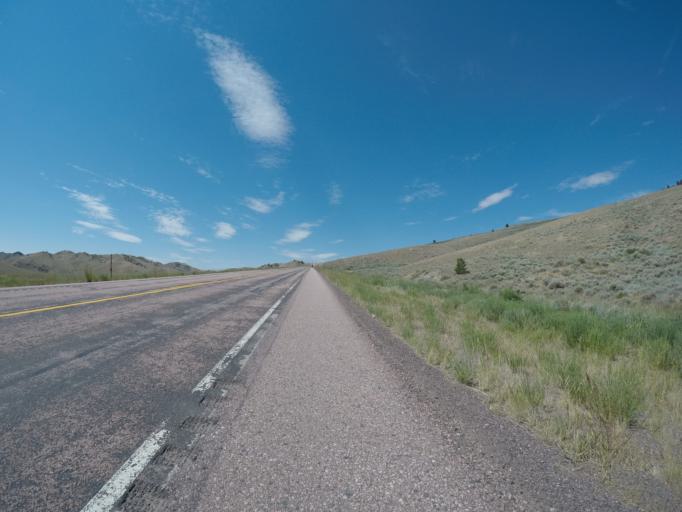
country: US
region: Wyoming
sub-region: Albany County
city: Laramie
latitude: 41.6896
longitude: -105.5126
